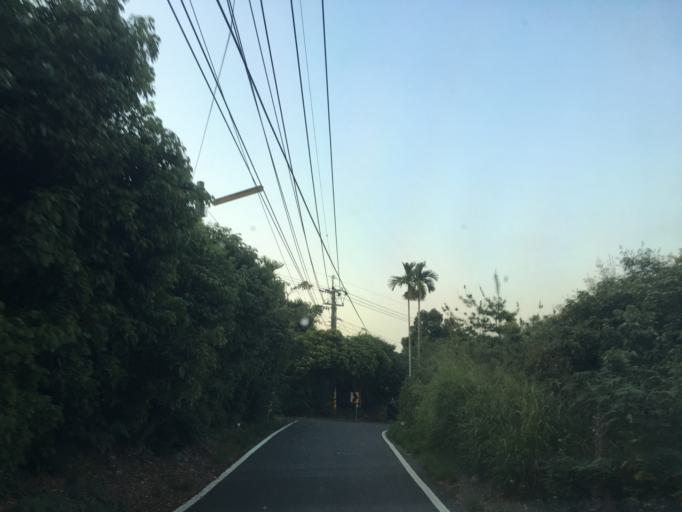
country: TW
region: Taiwan
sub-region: Nantou
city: Nantou
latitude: 23.9457
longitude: 120.6543
